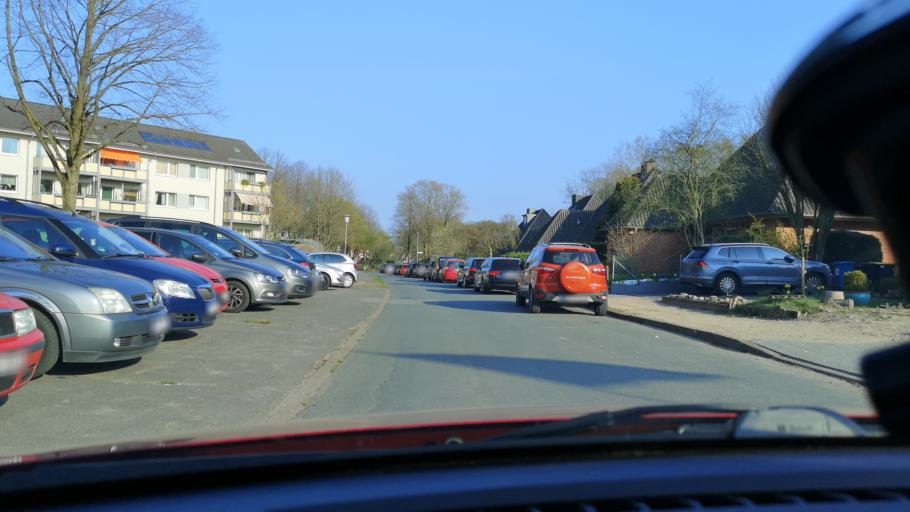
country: DE
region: Schleswig-Holstein
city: Ahrensburg
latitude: 53.6685
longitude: 10.2109
